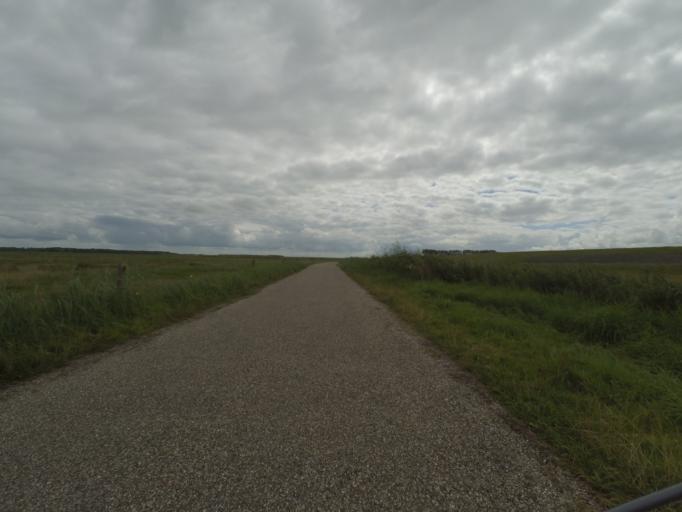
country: NL
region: Friesland
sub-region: Gemeente Dongeradeel
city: Anjum
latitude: 53.3409
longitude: 6.1531
